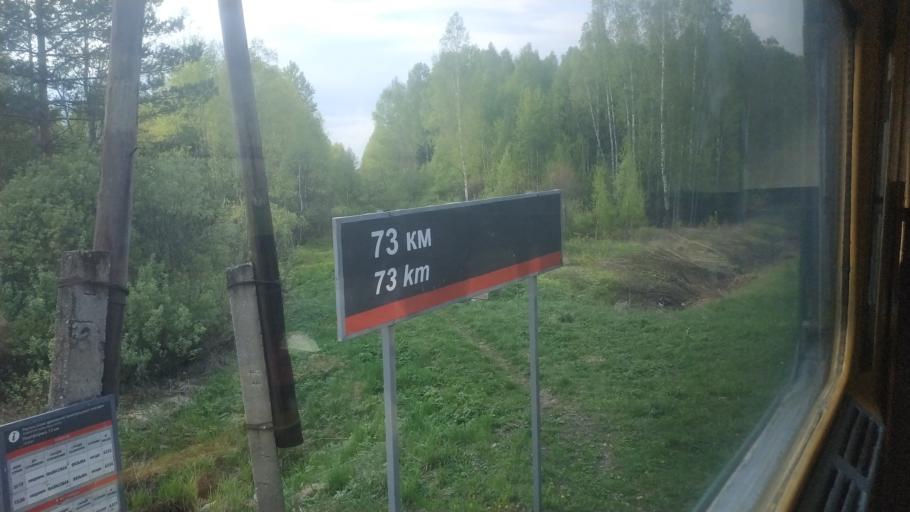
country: RU
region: Smolensk
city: Ugra
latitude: 54.5727
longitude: 34.3416
